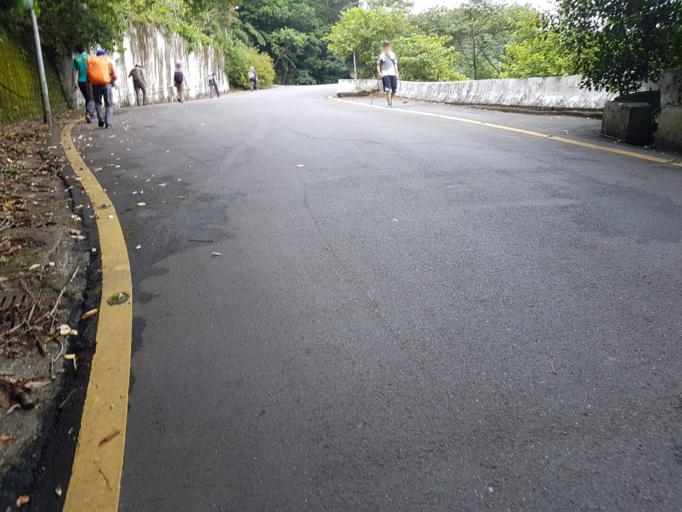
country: TW
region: Taiwan
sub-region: Keelung
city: Keelung
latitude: 25.0511
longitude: 121.6653
